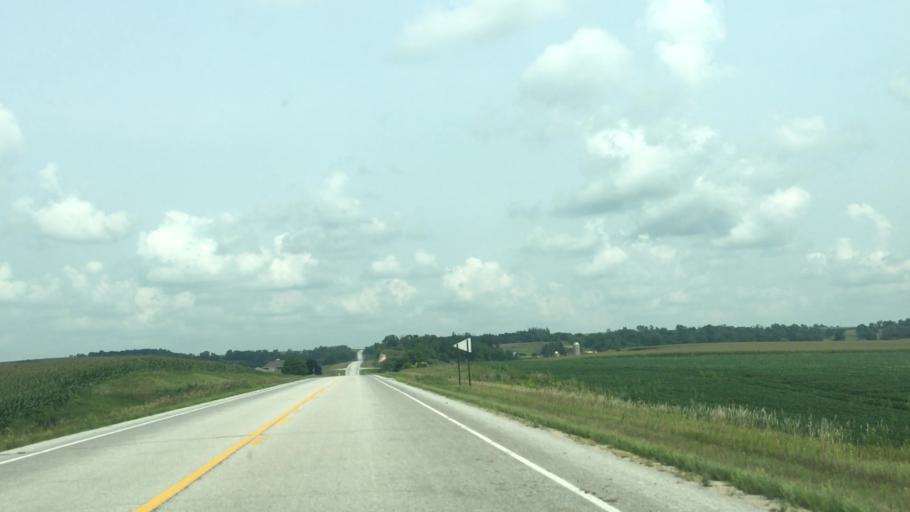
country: US
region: Minnesota
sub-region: Fillmore County
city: Harmony
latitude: 43.6206
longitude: -91.9299
